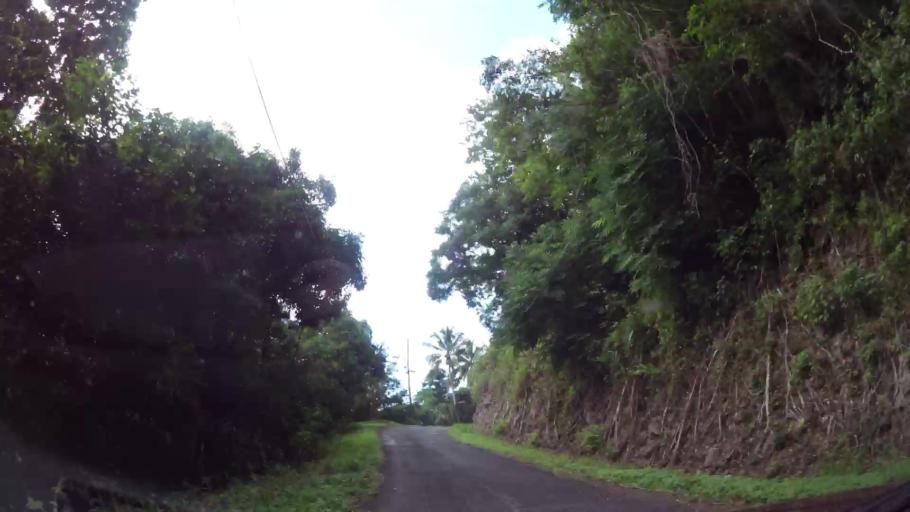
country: DM
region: Saint John
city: Portsmouth
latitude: 15.6228
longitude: -61.4611
